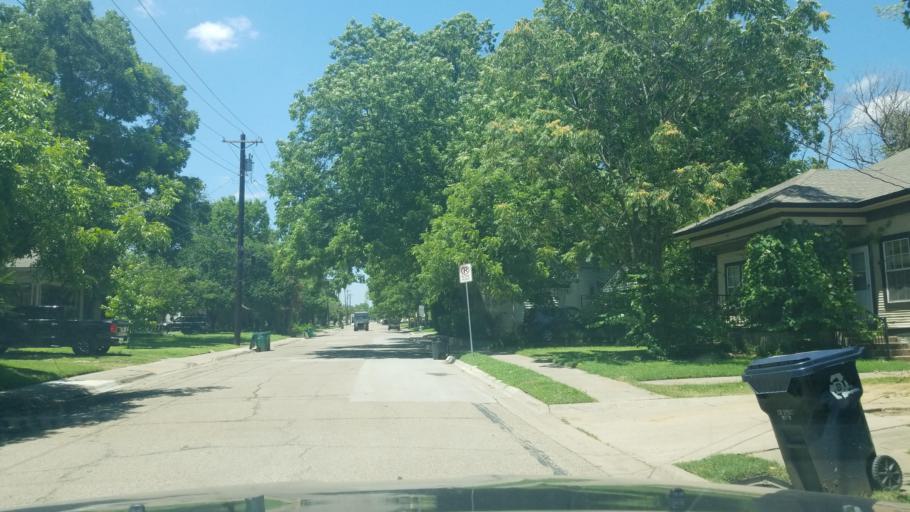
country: US
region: Texas
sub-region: Denton County
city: Denton
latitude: 33.2216
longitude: -97.1300
